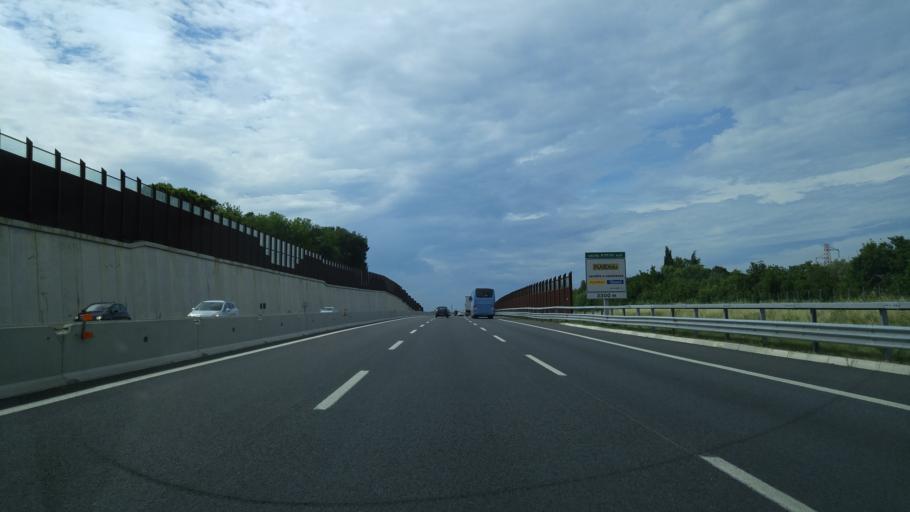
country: IT
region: Emilia-Romagna
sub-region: Provincia di Rimini
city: Rivazzurra
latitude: 44.0184
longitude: 12.5858
